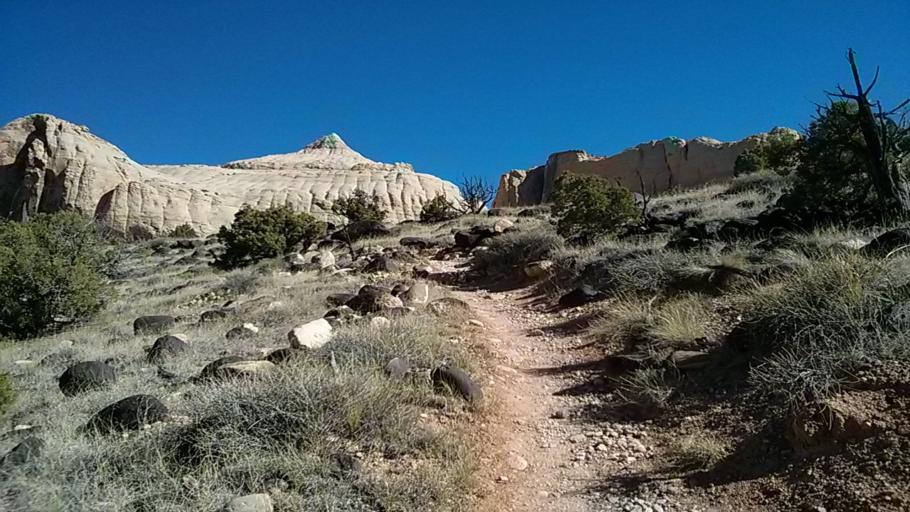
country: US
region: Utah
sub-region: Wayne County
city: Loa
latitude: 38.2896
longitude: -111.2263
